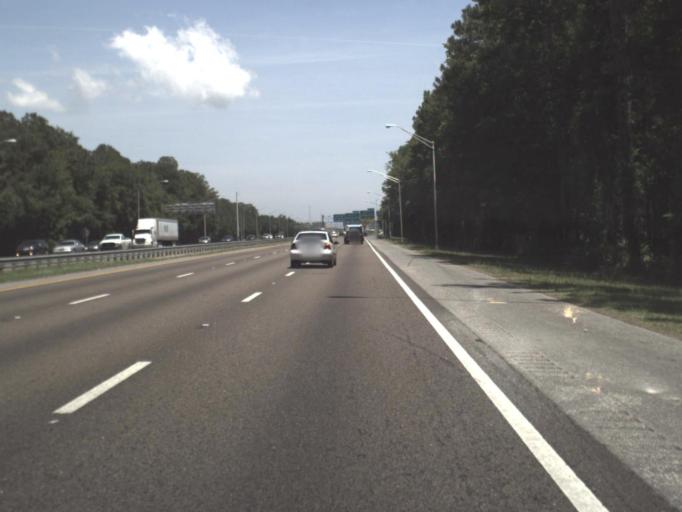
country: US
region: Florida
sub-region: Saint Johns County
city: Fruit Cove
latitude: 30.1678
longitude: -81.5814
